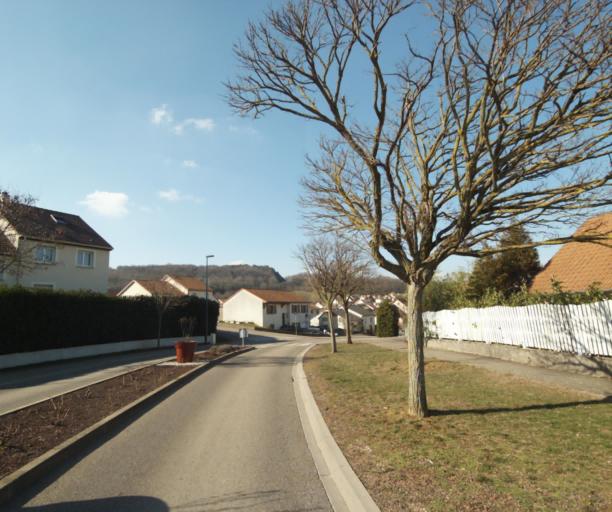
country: FR
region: Lorraine
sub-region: Departement de Meurthe-et-Moselle
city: Vandoeuvre-les-Nancy
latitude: 48.6367
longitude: 6.1788
